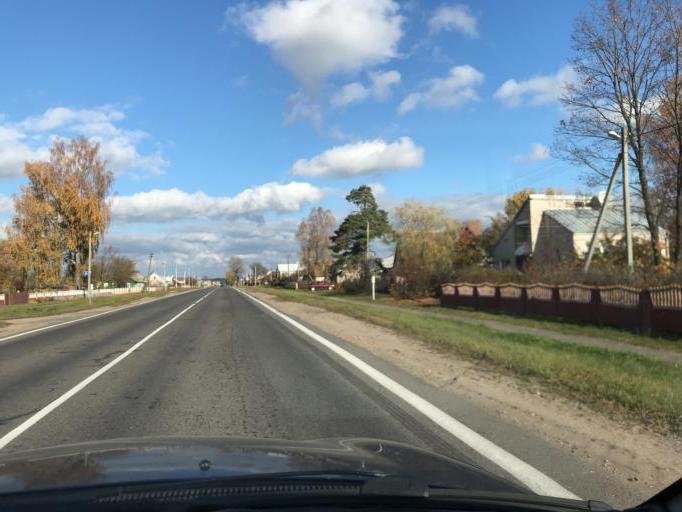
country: LT
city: Salcininkai
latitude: 54.2416
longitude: 25.3549
